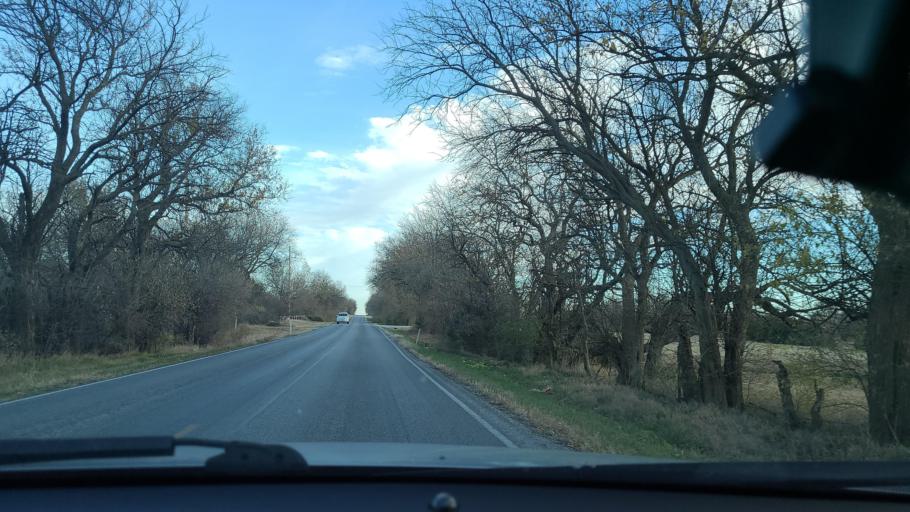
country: US
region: Kansas
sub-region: Sedgwick County
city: Goddard
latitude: 37.6497
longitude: -97.5516
